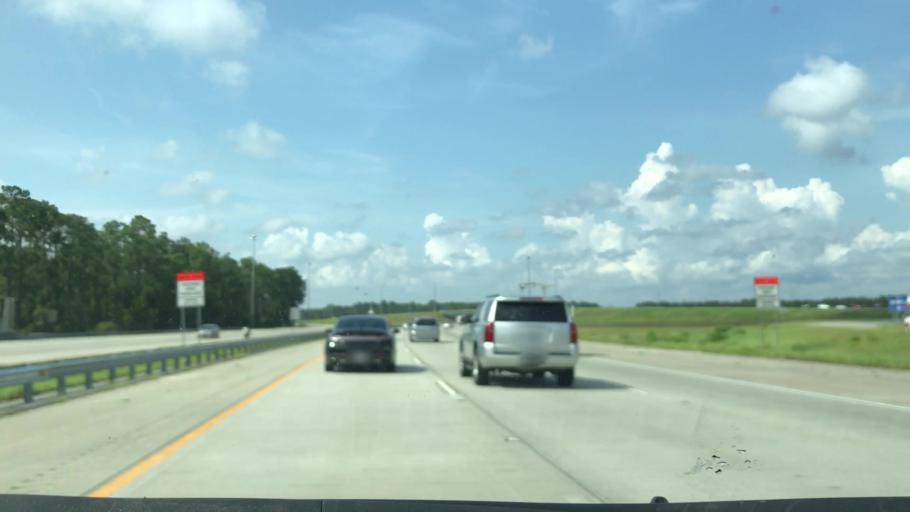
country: US
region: Georgia
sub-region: Glynn County
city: Dock Junction
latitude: 31.2461
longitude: -81.5003
